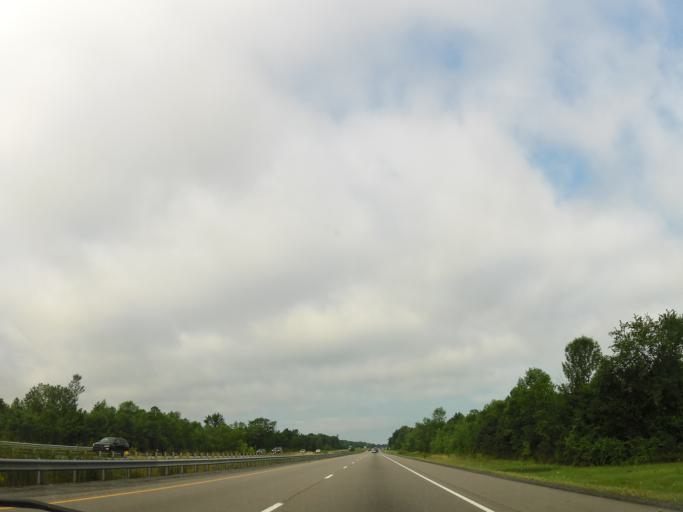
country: CA
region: Ontario
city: Skatepark
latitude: 44.2747
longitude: -76.8787
